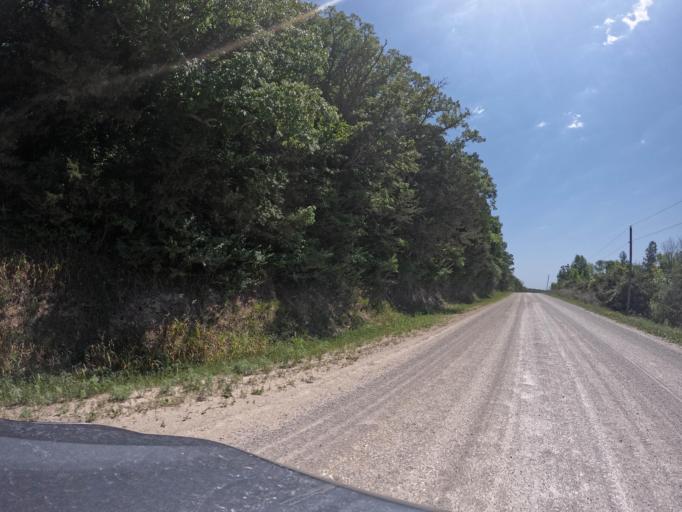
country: US
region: Iowa
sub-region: Henry County
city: Mount Pleasant
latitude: 40.8938
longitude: -91.5464
